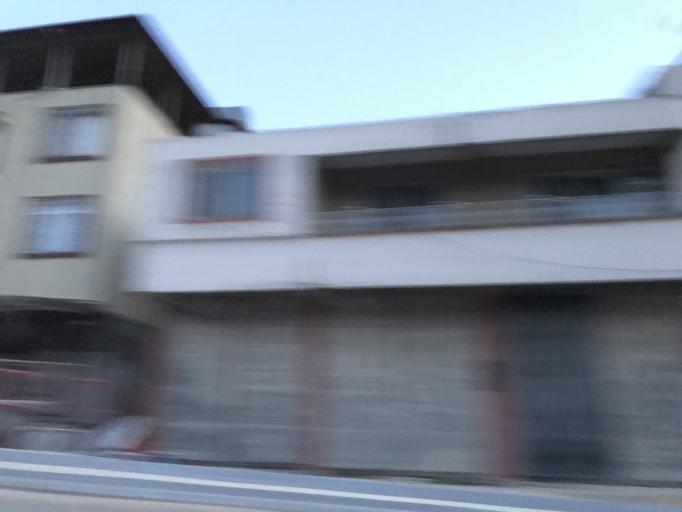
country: TR
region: Hatay
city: Karacay
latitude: 36.1454
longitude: 36.0738
